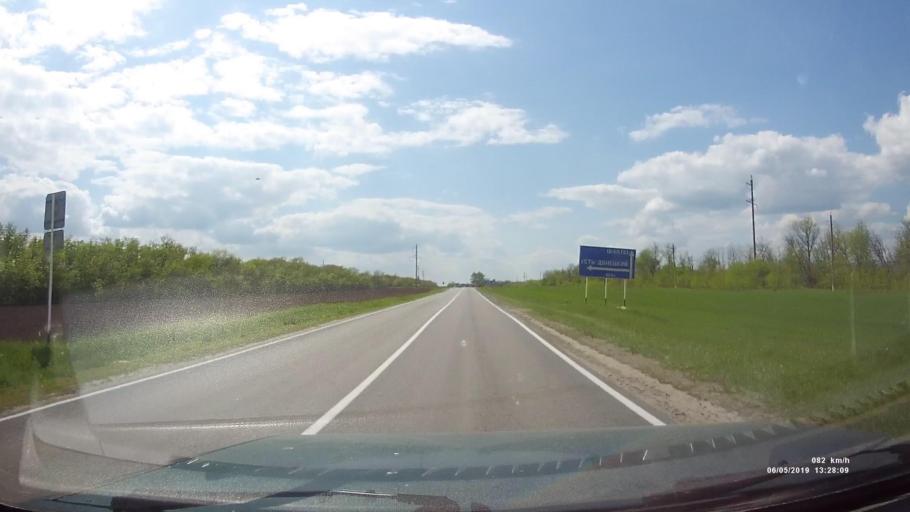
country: RU
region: Rostov
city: Ust'-Donetskiy
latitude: 47.6705
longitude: 40.8677
